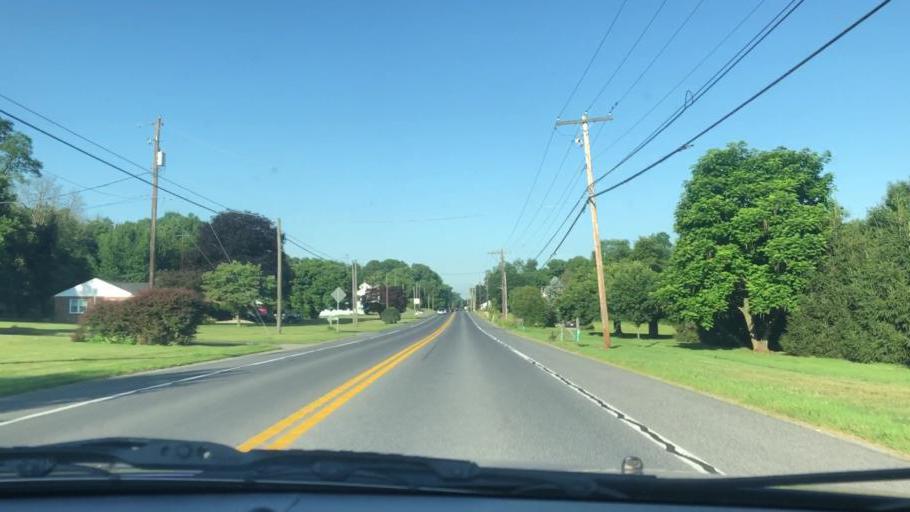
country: US
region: Pennsylvania
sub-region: Cumberland County
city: Carlisle
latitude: 40.1803
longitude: -77.2652
